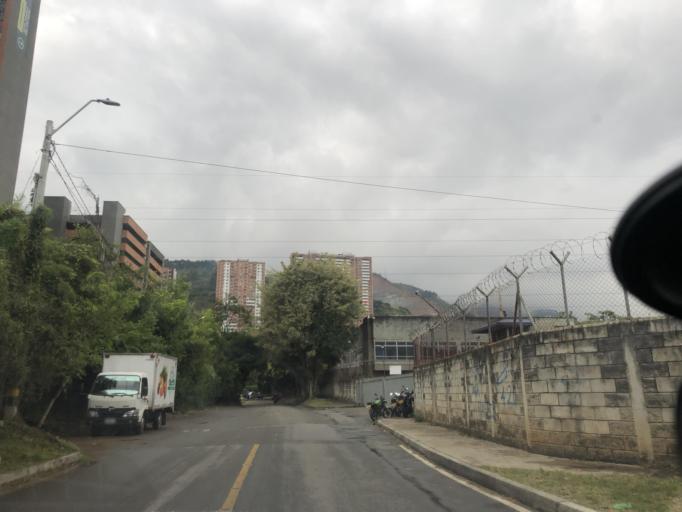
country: CO
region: Antioquia
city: Bello
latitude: 6.3262
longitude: -75.5512
